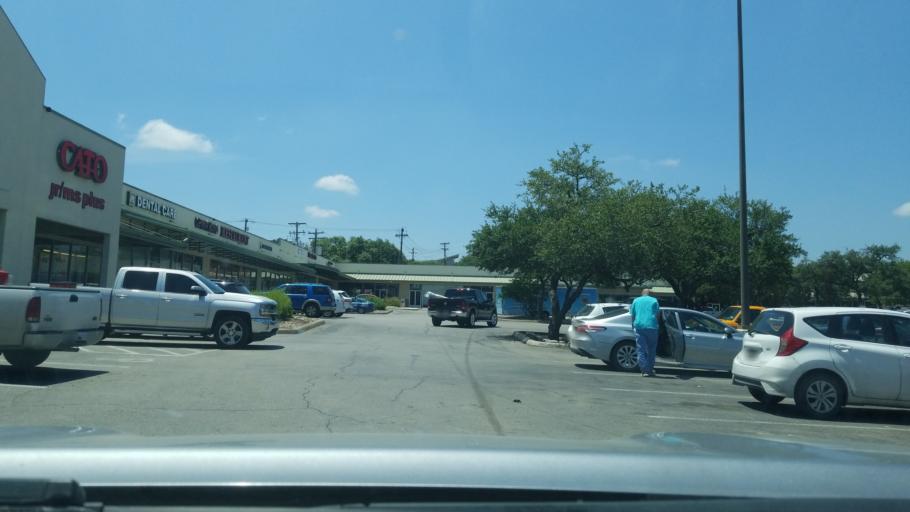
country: US
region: Texas
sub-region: Comal County
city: Bulverde
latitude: 29.7965
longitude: -98.4264
